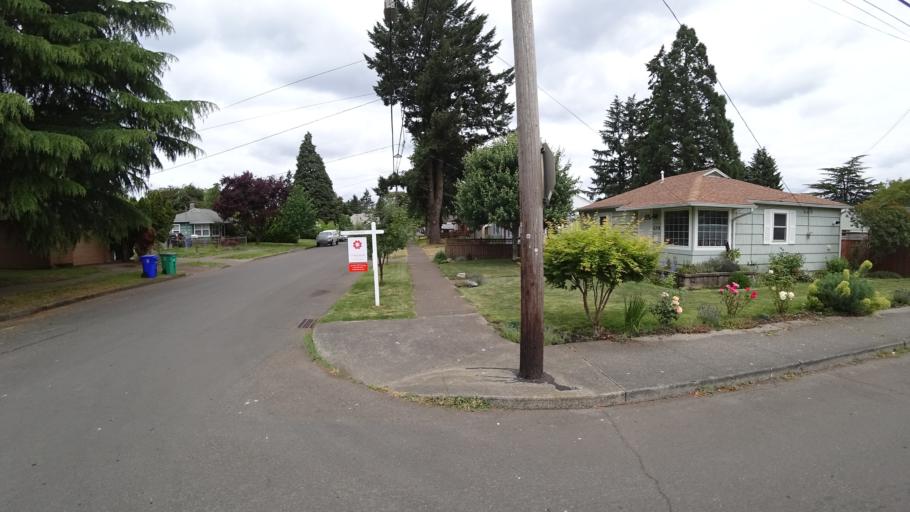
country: US
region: Oregon
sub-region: Multnomah County
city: Lents
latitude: 45.4748
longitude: -122.5707
